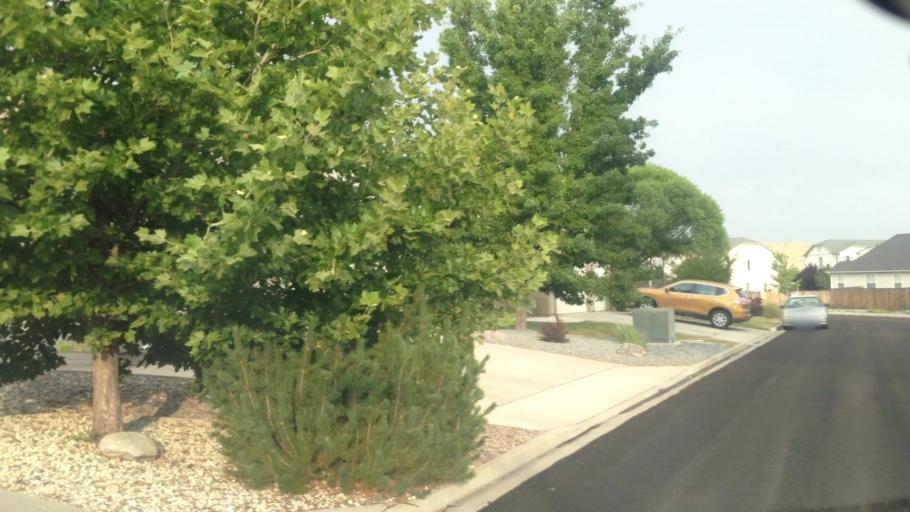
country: US
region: Nevada
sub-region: Washoe County
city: Lemmon Valley
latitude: 39.6335
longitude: -119.8720
